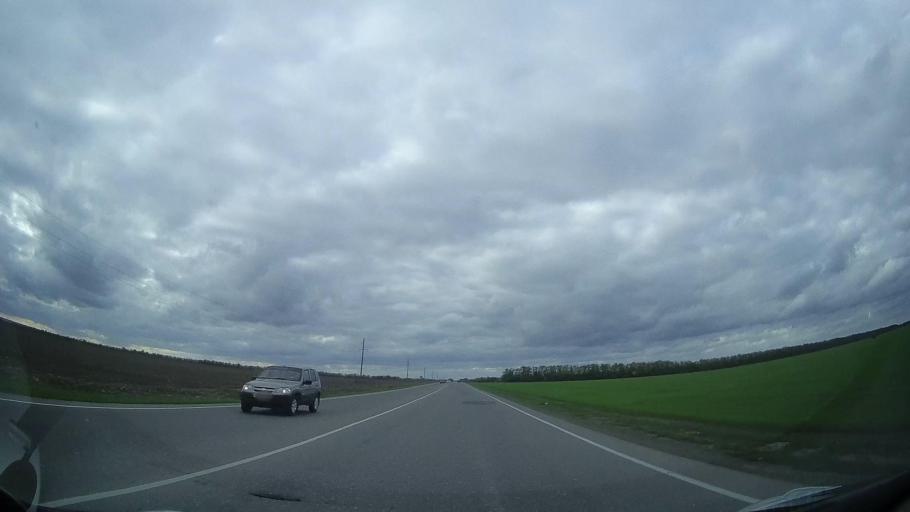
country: RU
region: Rostov
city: Mechetinskaya
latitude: 46.7890
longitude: 40.4029
